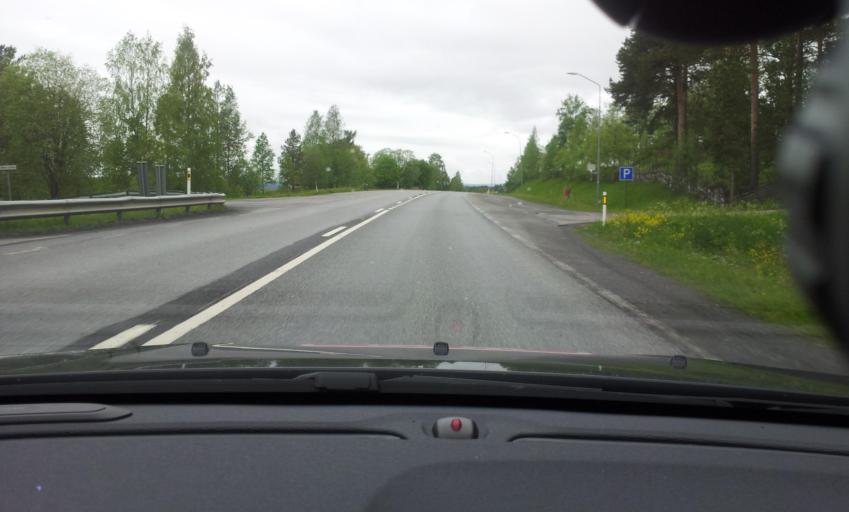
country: SE
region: Jaemtland
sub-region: Krokoms Kommun
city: Krokom
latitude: 63.3147
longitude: 14.0991
